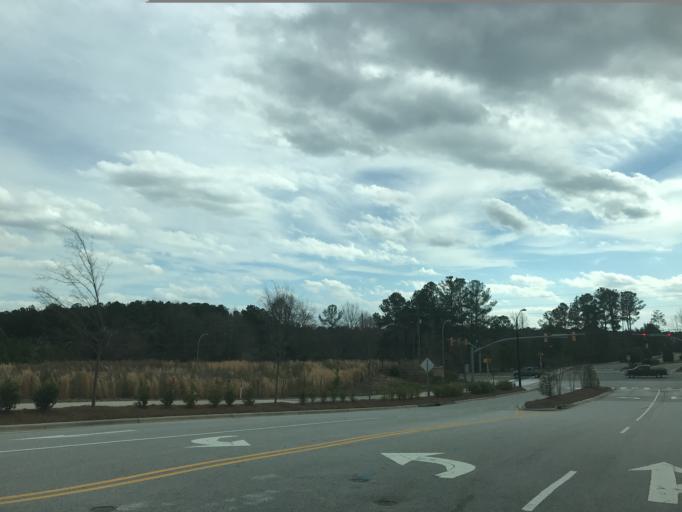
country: US
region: North Carolina
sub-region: Wake County
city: Morrisville
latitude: 35.7932
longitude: -78.8437
